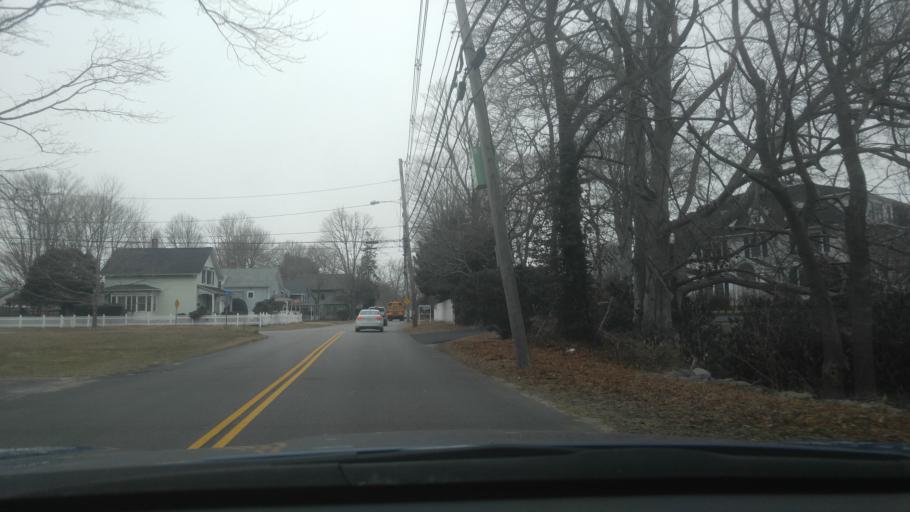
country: US
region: Rhode Island
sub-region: Washington County
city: Wakefield-Peacedale
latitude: 41.4360
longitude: -71.4946
